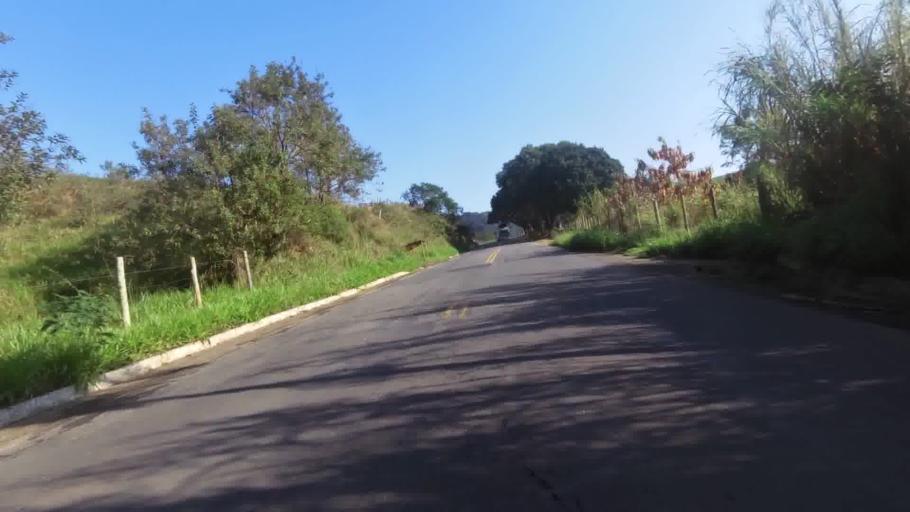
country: BR
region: Espirito Santo
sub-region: Alfredo Chaves
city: Alfredo Chaves
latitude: -20.6623
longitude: -40.7093
